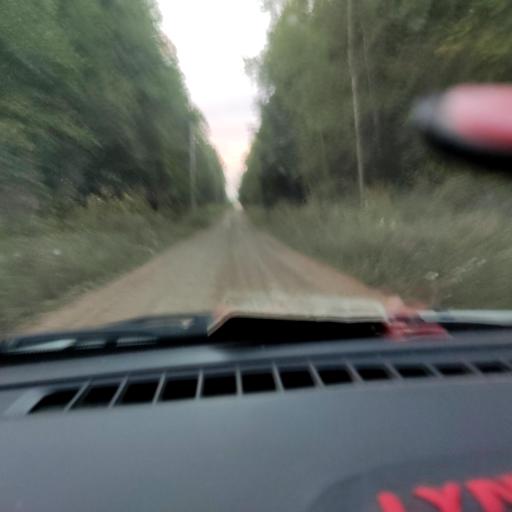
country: RU
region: Perm
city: Kukushtan
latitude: 57.6197
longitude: 56.4750
